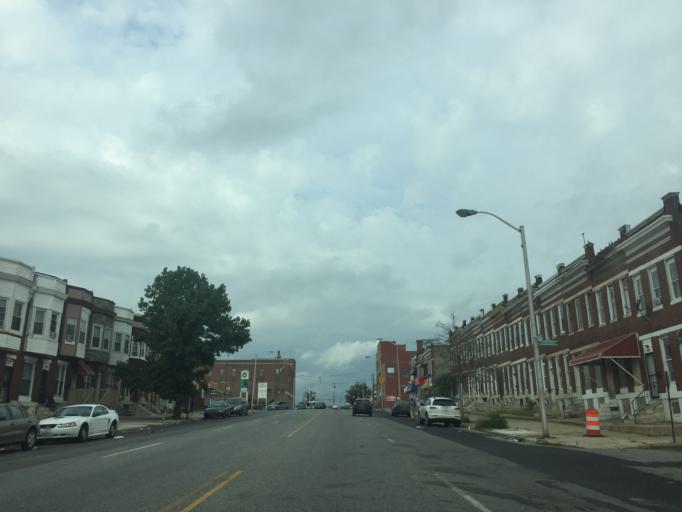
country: US
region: Maryland
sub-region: Baltimore County
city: Lansdowne
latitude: 39.2945
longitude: -76.6619
